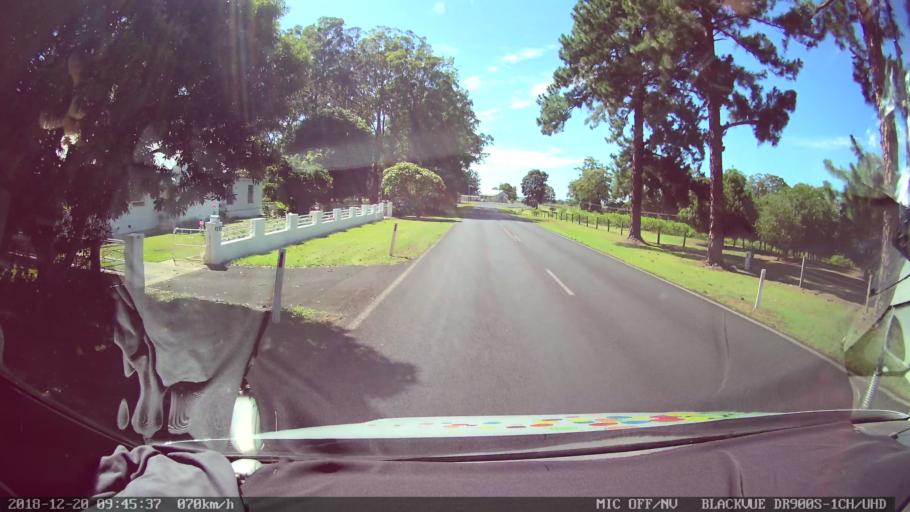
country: AU
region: New South Wales
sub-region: Lismore Municipality
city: Lismore
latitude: -28.7453
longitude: 153.3015
